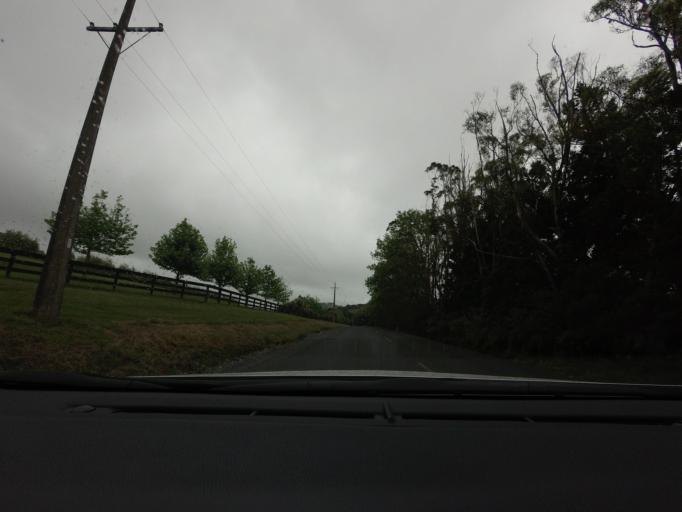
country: NZ
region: Auckland
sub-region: Auckland
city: Wellsford
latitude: -36.2848
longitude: 174.6122
